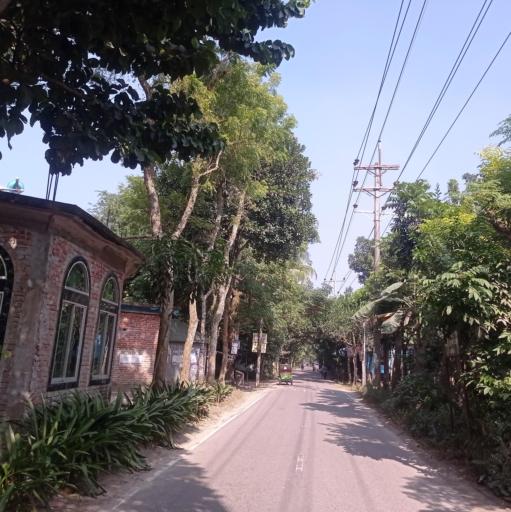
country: BD
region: Dhaka
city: Narsingdi
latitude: 24.0379
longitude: 90.6766
